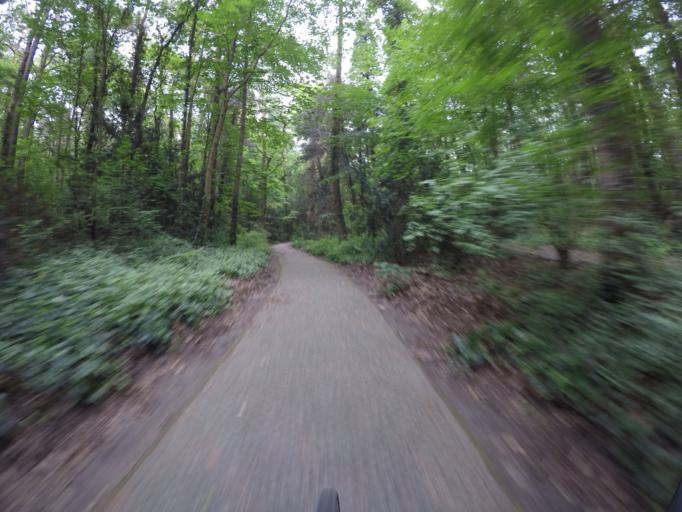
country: DE
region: Berlin
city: Waidmannslust
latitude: 52.5996
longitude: 13.3087
